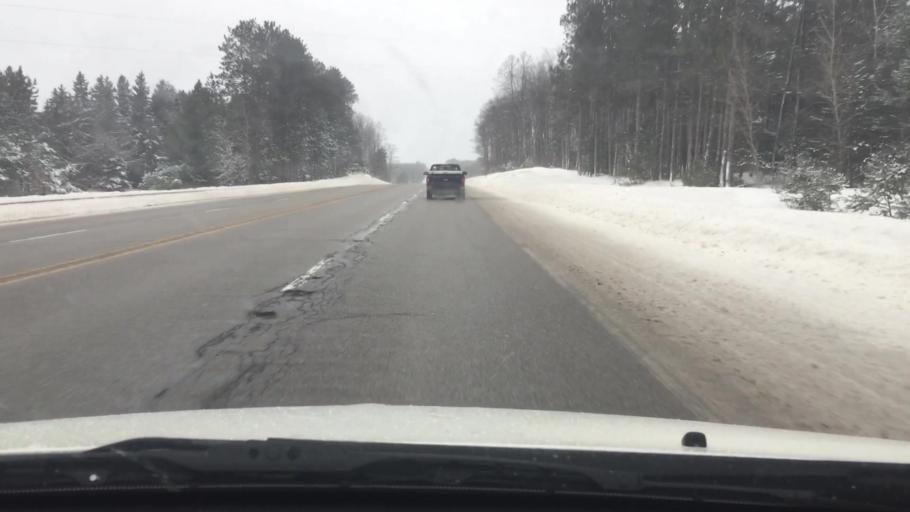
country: US
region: Michigan
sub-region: Otsego County
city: Gaylord
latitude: 45.0465
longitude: -84.7758
